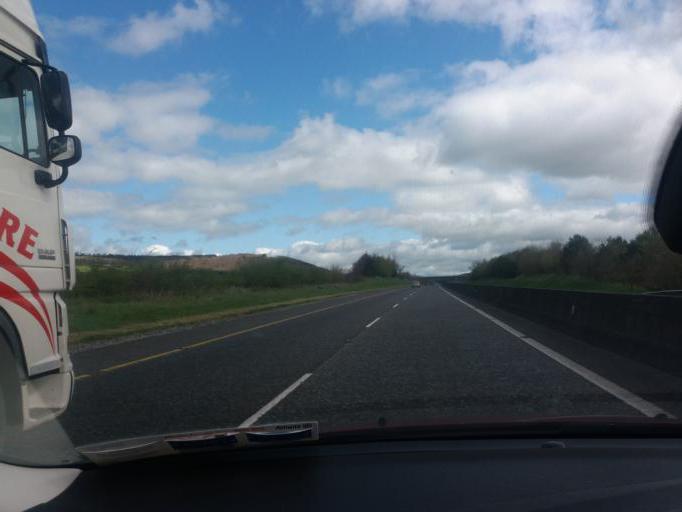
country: IE
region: Munster
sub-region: County Cork
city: Rathcormac
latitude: 52.0936
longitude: -8.2890
